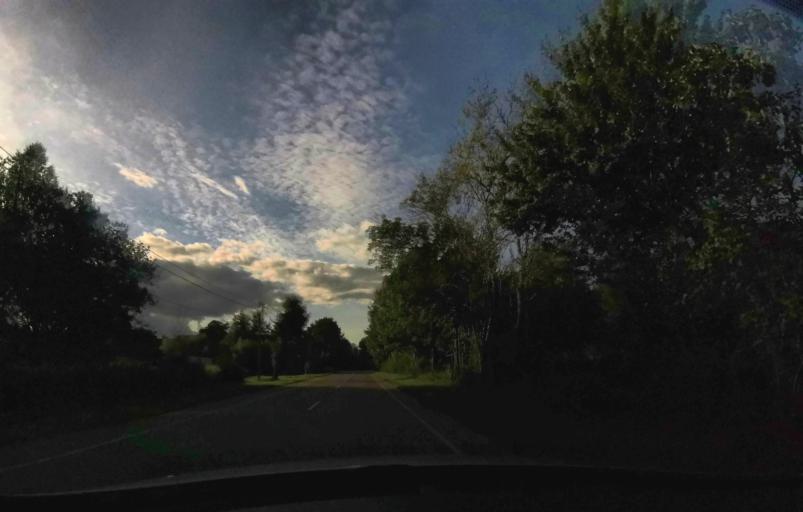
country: RU
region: Kaliningrad
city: Chernyakhovsk
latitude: 54.6233
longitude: 21.8206
